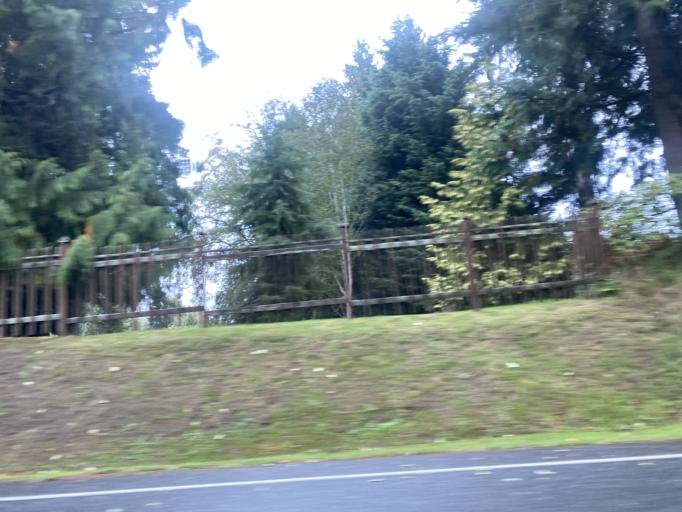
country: US
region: Washington
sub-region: Island County
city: Langley
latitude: 48.0401
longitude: -122.4220
